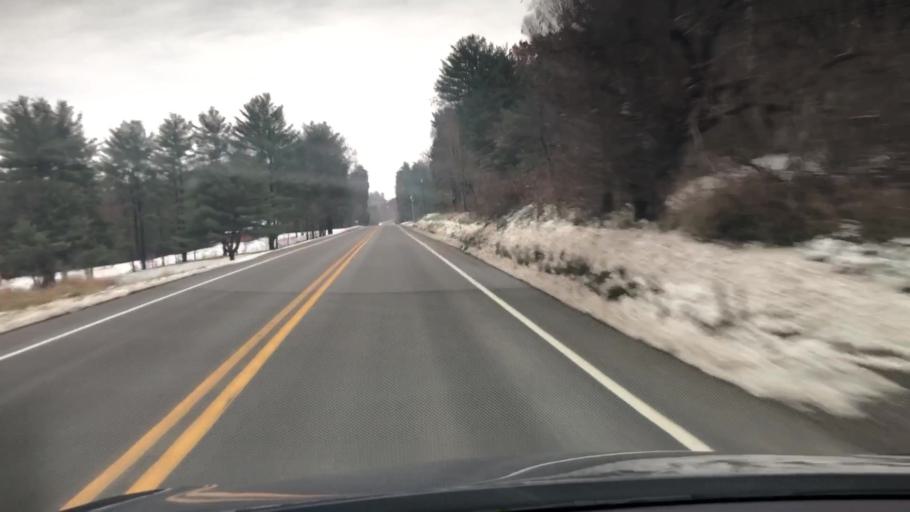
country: US
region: Pennsylvania
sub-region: Jefferson County
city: Brookville
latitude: 41.0454
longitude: -79.2539
